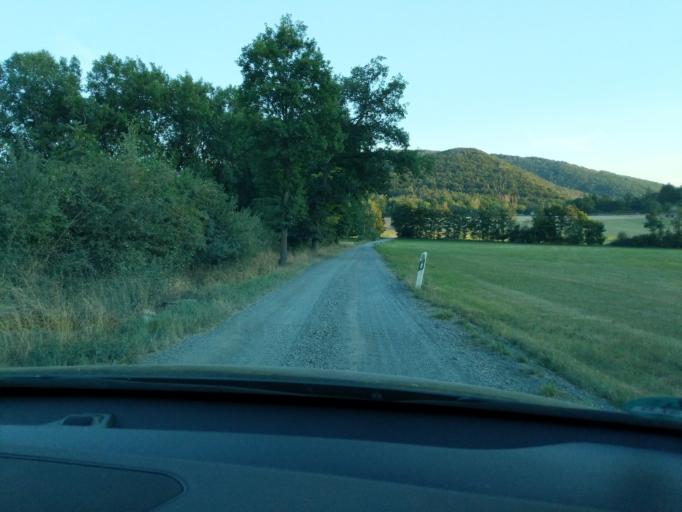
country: DE
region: Hesse
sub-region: Regierungsbezirk Kassel
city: Waldeck
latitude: 51.1853
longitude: 9.0313
